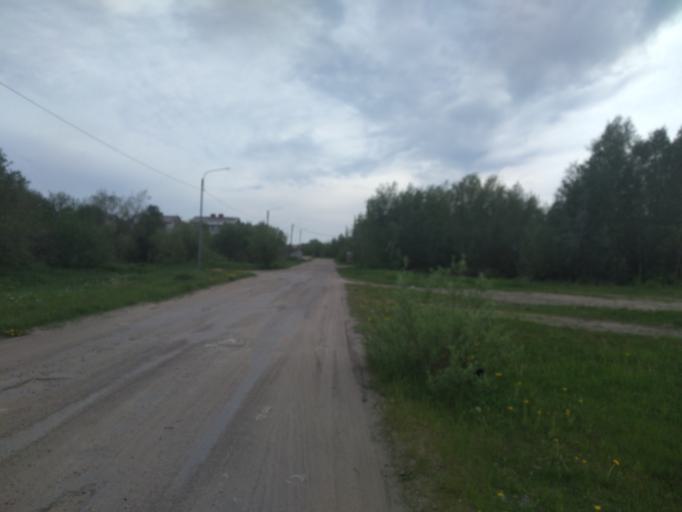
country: RU
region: Komi Republic
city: Pechora
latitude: 65.1424
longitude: 57.2468
